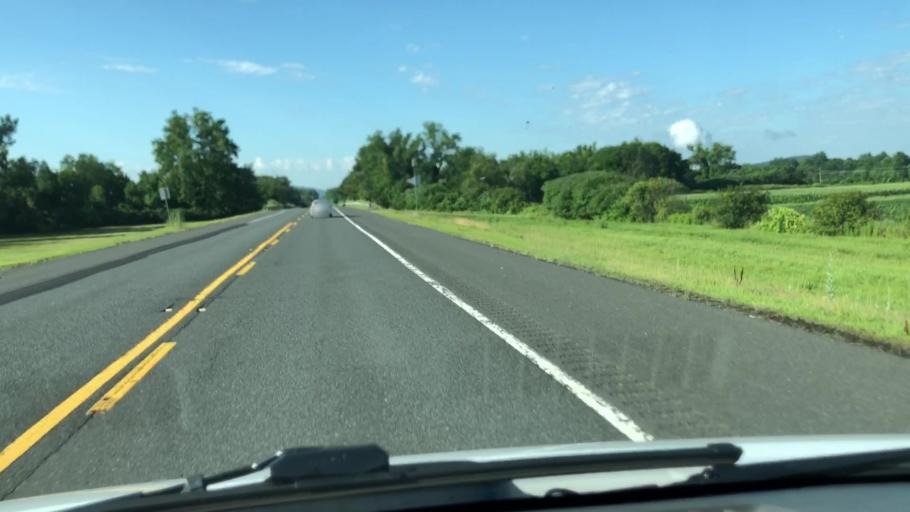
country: US
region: Massachusetts
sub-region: Hampshire County
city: North Amherst
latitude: 42.4170
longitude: -72.5370
